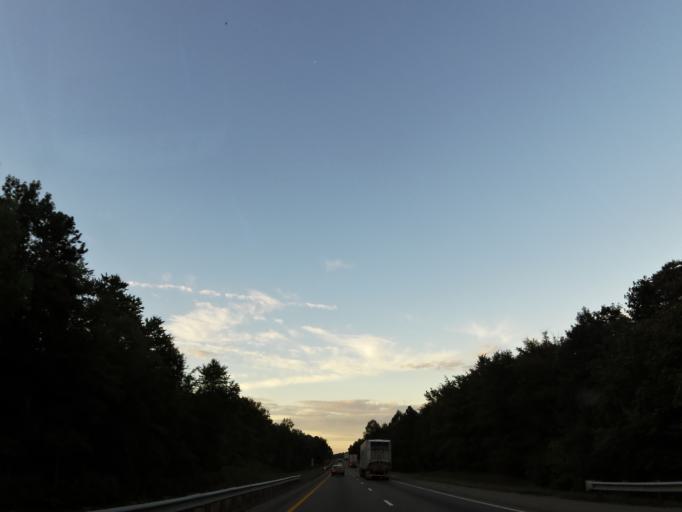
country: US
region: Tennessee
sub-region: McMinn County
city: Athens
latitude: 35.3999
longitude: -84.7107
